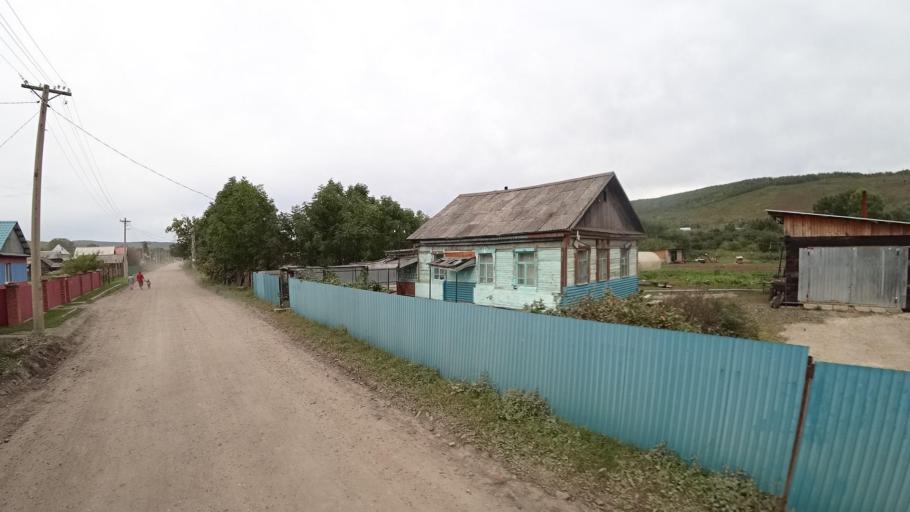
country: RU
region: Jewish Autonomous Oblast
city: Khingansk
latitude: 49.0326
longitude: 131.0492
